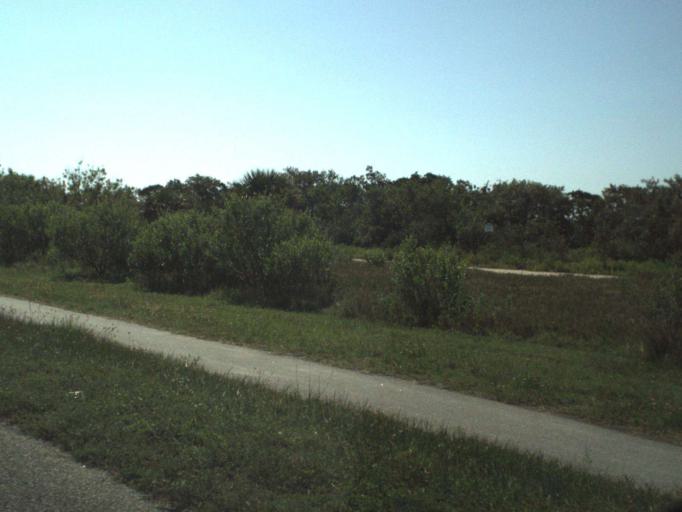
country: US
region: Florida
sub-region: Brevard County
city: Cocoa Beach
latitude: 28.3576
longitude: -80.6317
